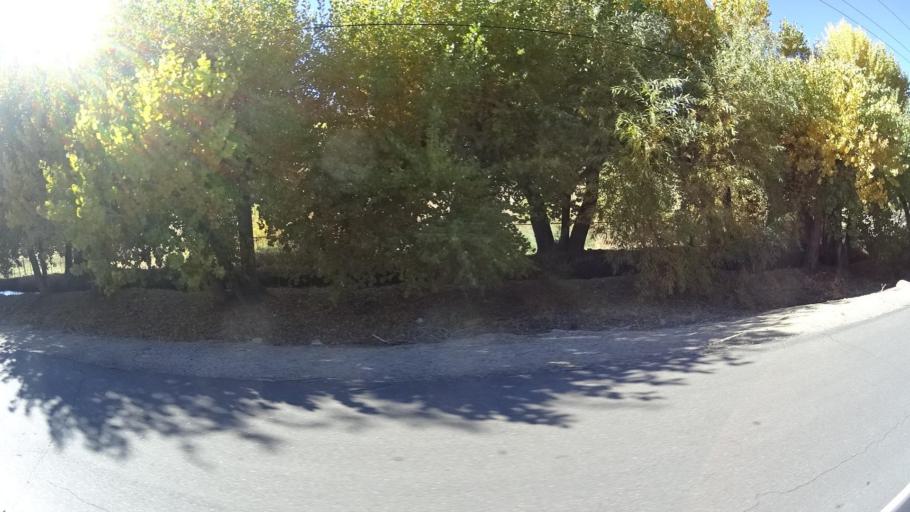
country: US
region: California
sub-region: Kern County
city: Kernville
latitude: 35.7465
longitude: -118.4139
